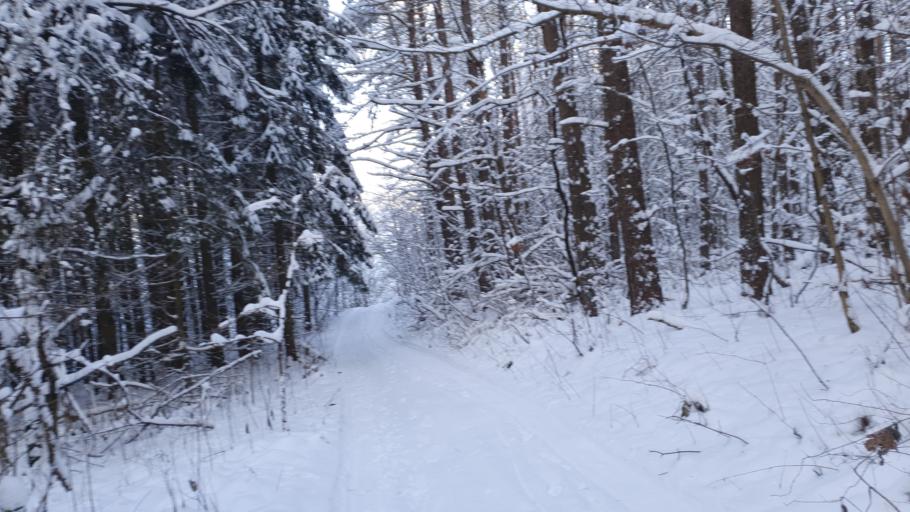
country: LT
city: Skaidiskes
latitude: 54.6411
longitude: 25.4161
